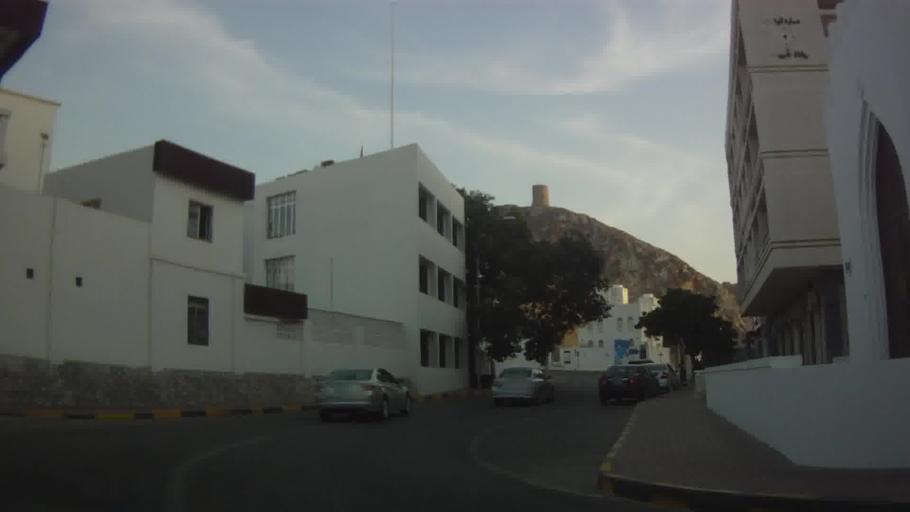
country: OM
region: Muhafazat Masqat
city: Muscat
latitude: 23.6142
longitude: 58.5896
